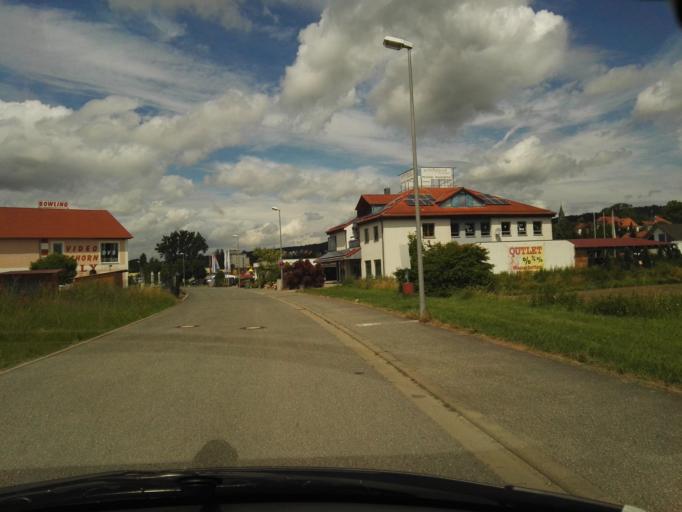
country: DE
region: Bavaria
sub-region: Upper Franconia
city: Burgkunstadt
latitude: 50.1354
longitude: 11.2526
